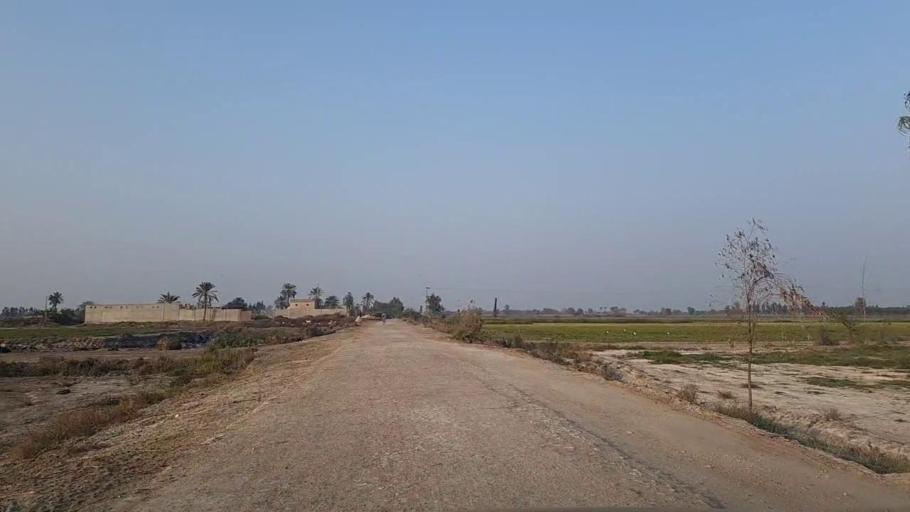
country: PK
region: Sindh
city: Daur
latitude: 26.4227
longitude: 68.3935
